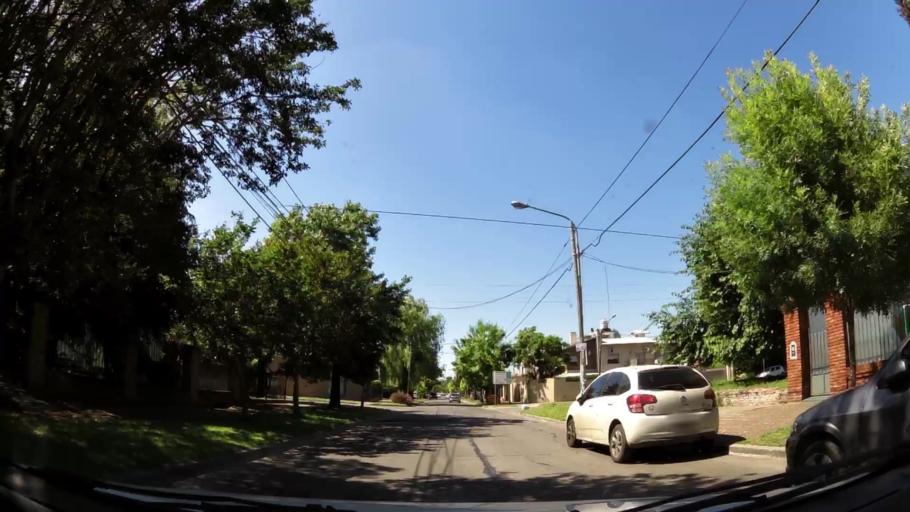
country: AR
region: Buenos Aires
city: Ituzaingo
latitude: -34.6519
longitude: -58.6627
